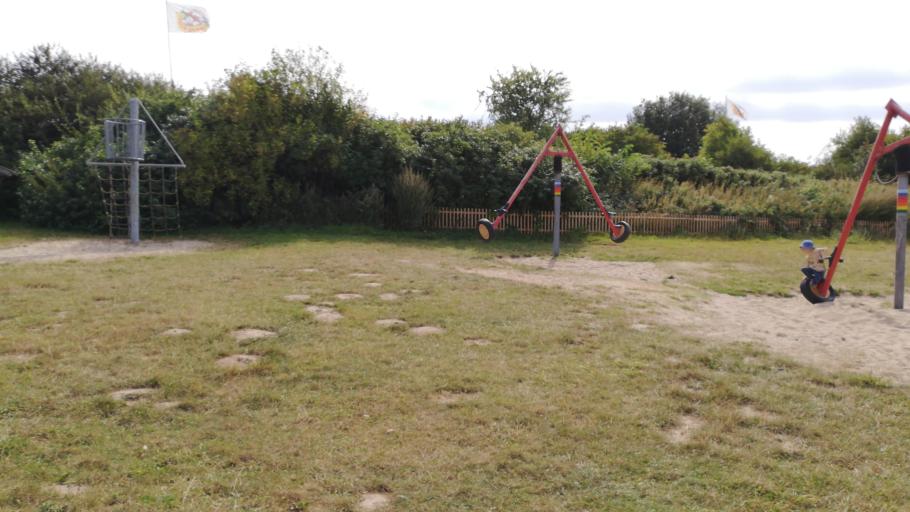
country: DE
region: Schleswig-Holstein
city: Tolk
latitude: 54.5750
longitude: 9.6302
